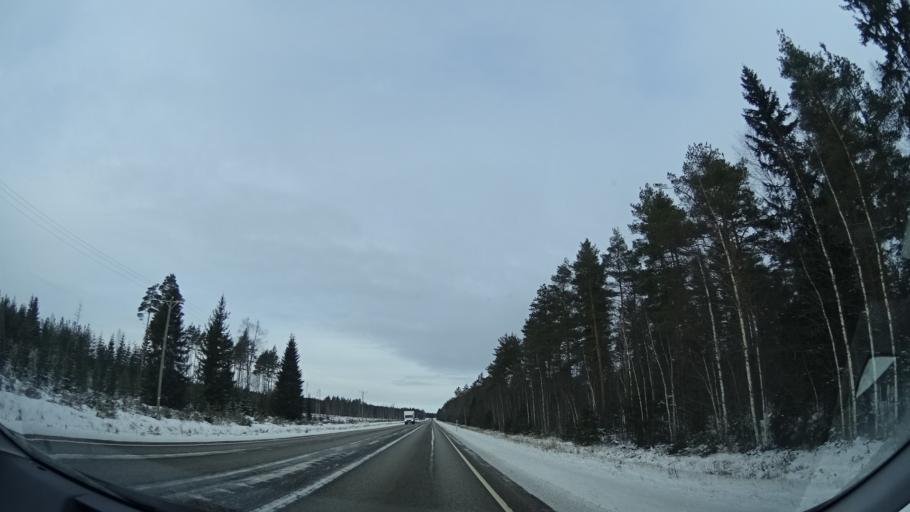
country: FI
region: Uusimaa
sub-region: Helsinki
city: Kaerkoelae
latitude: 60.6737
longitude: 23.8206
